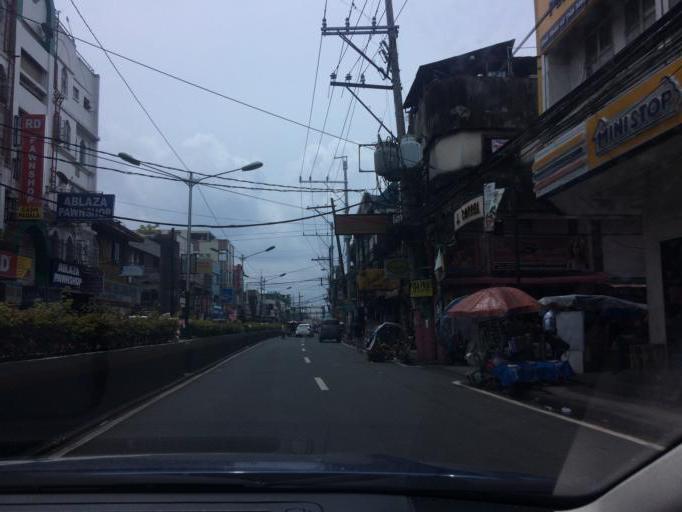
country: PH
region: Metro Manila
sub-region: Makati City
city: Makati City
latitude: 14.5286
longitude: 120.9972
